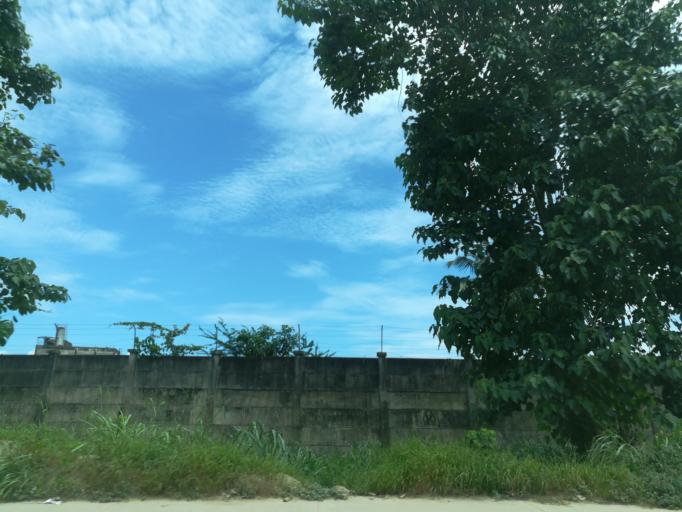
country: NG
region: Lagos
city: Ebute Ikorodu
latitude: 6.5710
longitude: 3.4832
